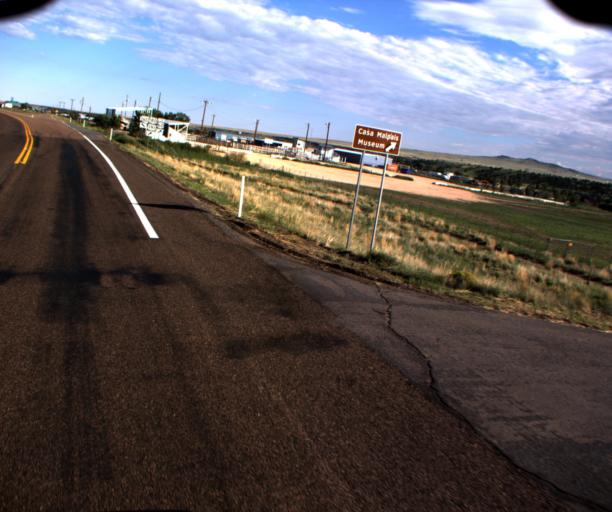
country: US
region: Arizona
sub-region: Apache County
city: Eagar
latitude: 34.1073
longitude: -109.2480
